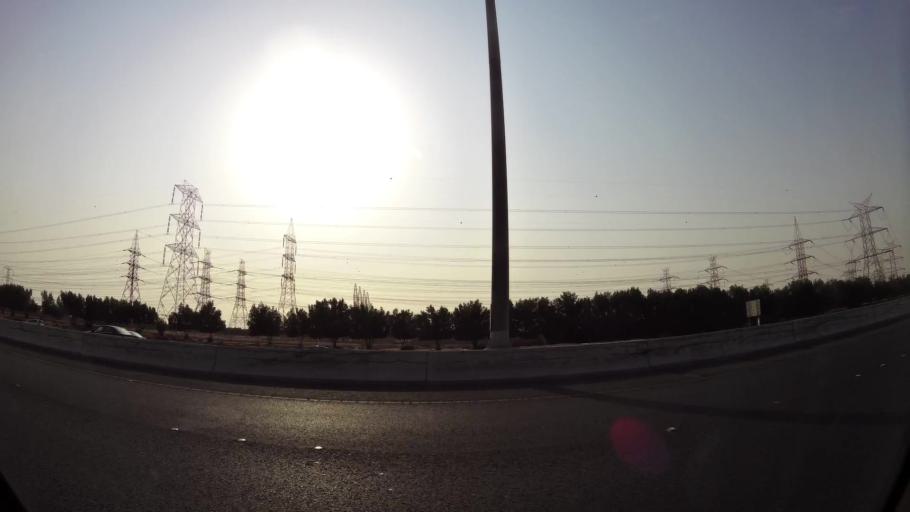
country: KW
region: Mubarak al Kabir
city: Sabah as Salim
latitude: 29.2598
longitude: 48.0442
